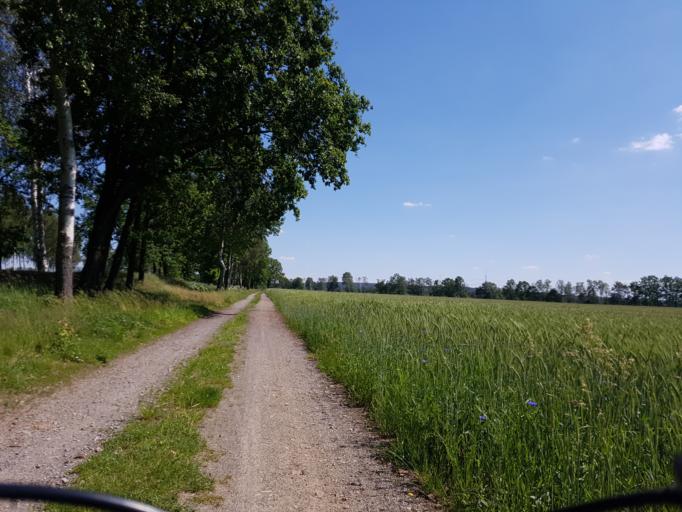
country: DE
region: Brandenburg
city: Elsterwerda
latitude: 51.4362
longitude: 13.5356
